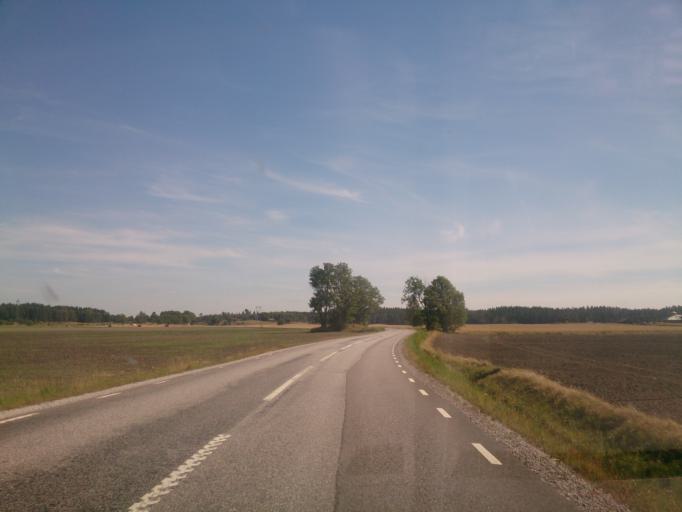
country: SE
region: OEstergoetland
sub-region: Norrkopings Kommun
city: Kimstad
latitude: 58.4830
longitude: 15.9932
